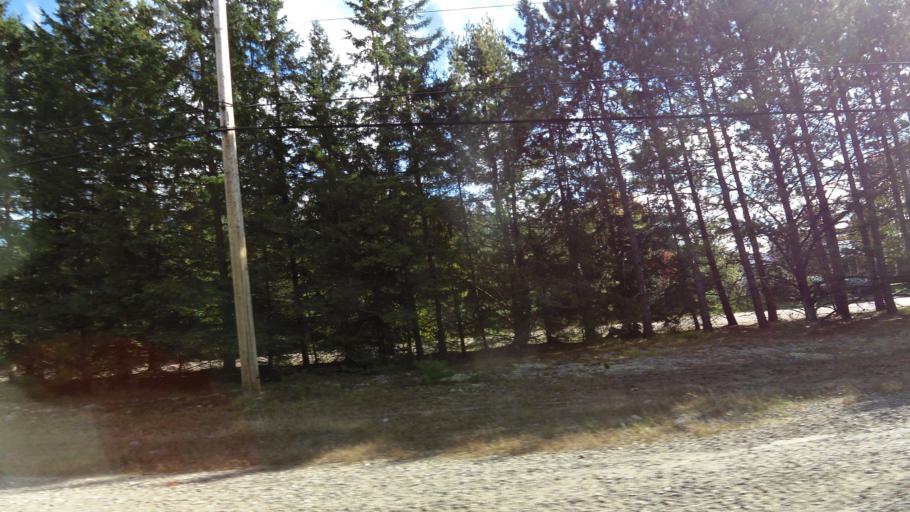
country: CA
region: Ontario
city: Deep River
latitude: 46.0664
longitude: -77.4748
